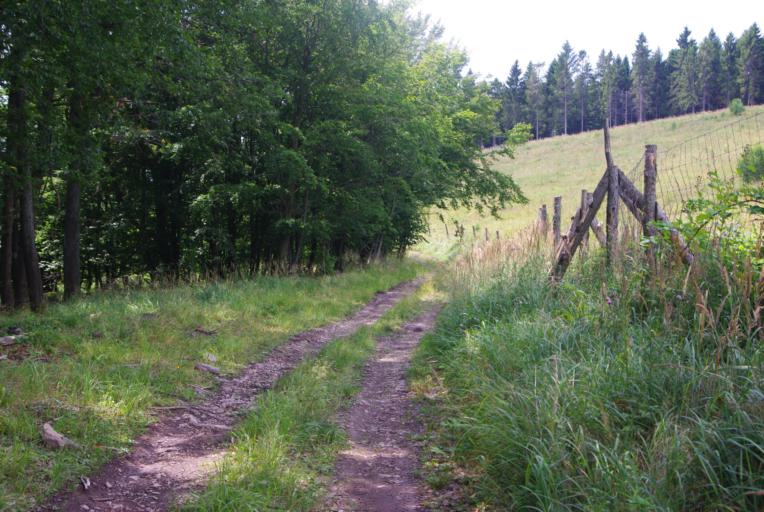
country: HU
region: Borsod-Abauj-Zemplen
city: Gonc
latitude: 48.4123
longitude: 21.3794
